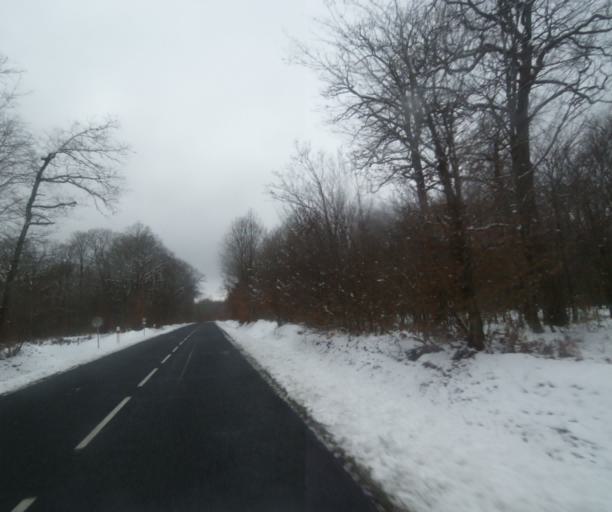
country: FR
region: Champagne-Ardenne
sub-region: Departement de la Haute-Marne
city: Laneuville-a-Remy
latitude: 48.4569
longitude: 4.8810
